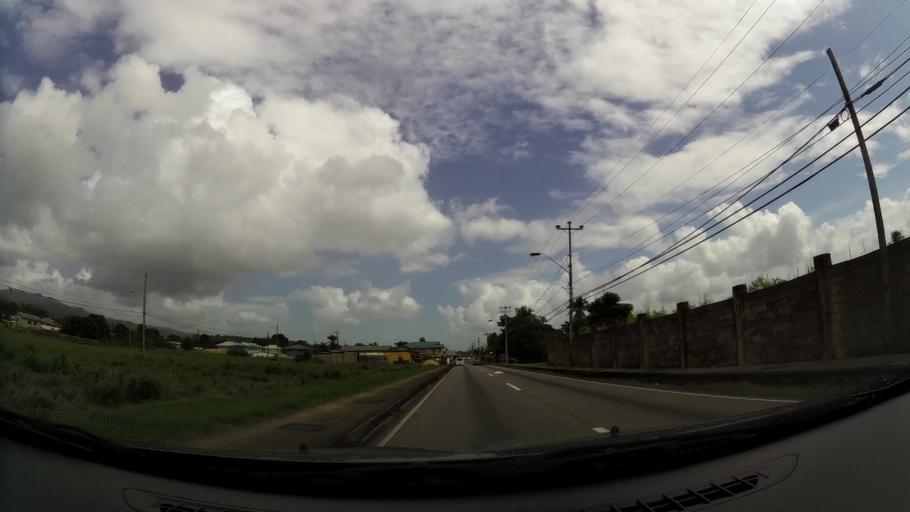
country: TT
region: Tunapuna/Piarco
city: Arouca
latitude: 10.6292
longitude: -61.3149
